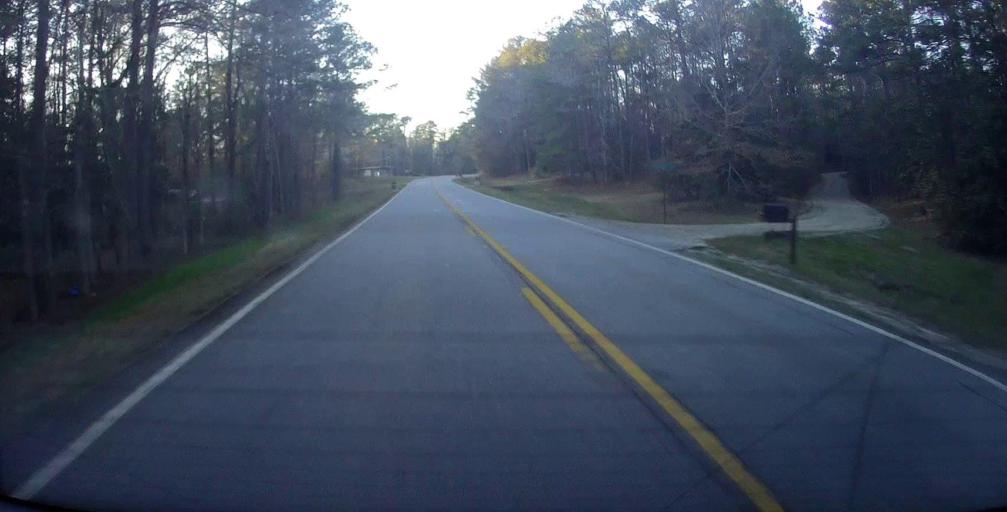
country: US
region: Alabama
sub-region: Lee County
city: Smiths Station
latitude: 32.6223
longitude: -85.0328
